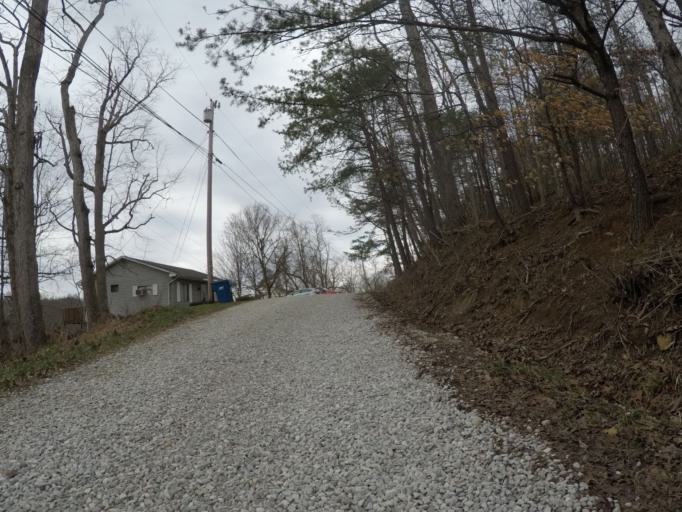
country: US
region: West Virginia
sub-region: Cabell County
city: Pea Ridge
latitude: 38.3882
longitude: -82.3831
